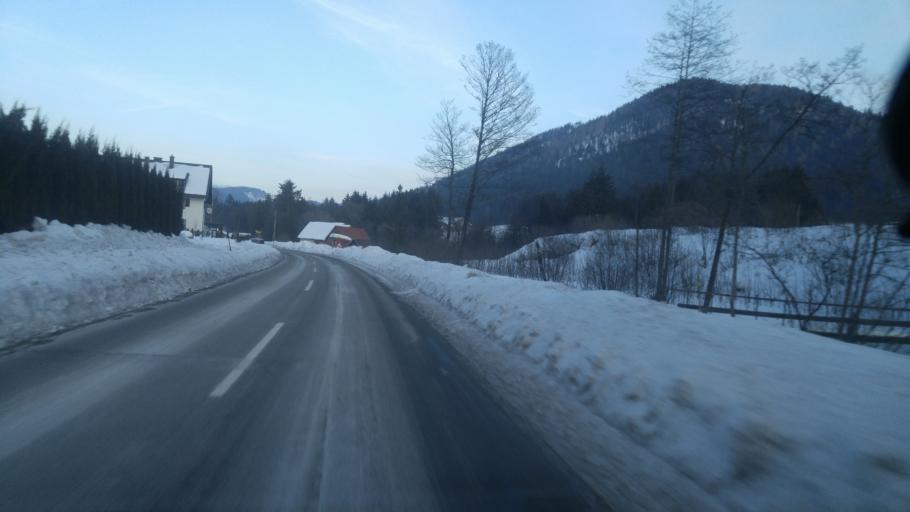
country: AT
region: Lower Austria
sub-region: Politischer Bezirk Wiener Neustadt
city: Rohr im Gebirge
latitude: 47.8800
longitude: 15.7090
